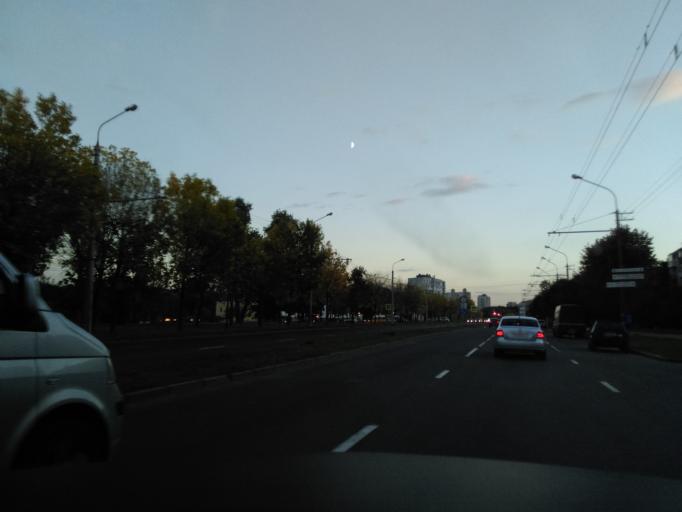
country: BY
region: Minsk
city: Minsk
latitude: 53.9221
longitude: 27.6377
